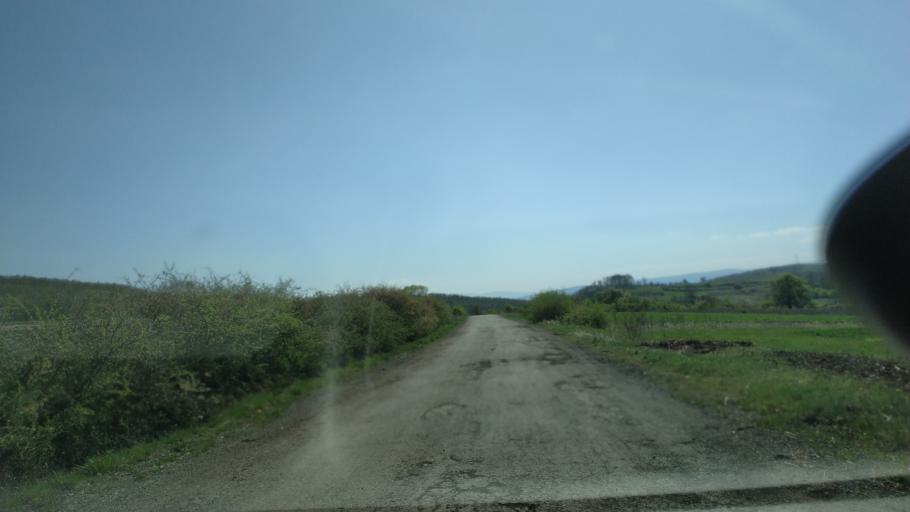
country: RS
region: Central Serbia
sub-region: Zajecarski Okrug
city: Soko Banja
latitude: 43.5138
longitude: 21.9047
